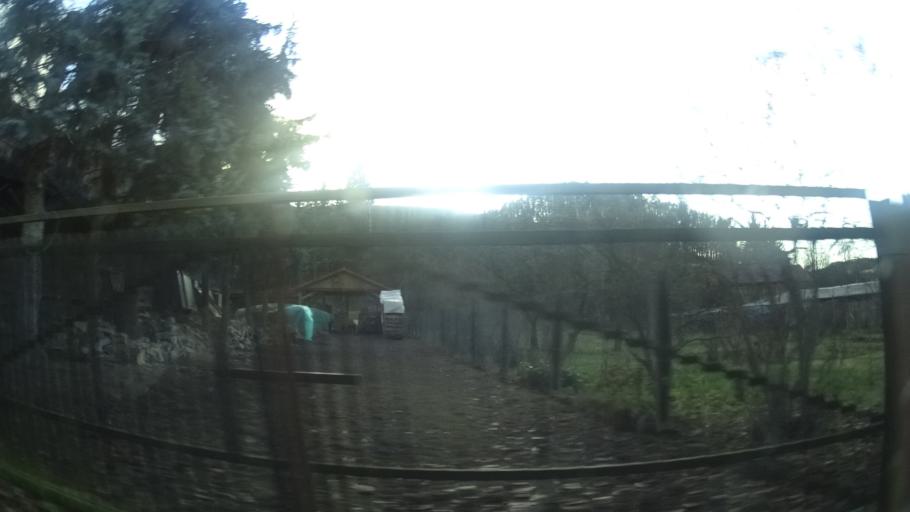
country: DE
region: Thuringia
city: Unterwellenborn
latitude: 50.6905
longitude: 11.4110
